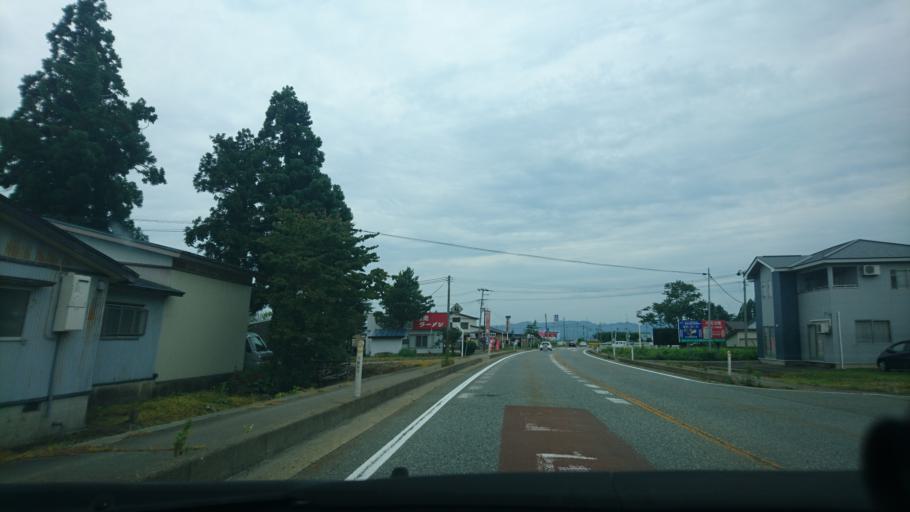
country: JP
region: Akita
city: Omagari
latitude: 39.4158
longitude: 140.5456
